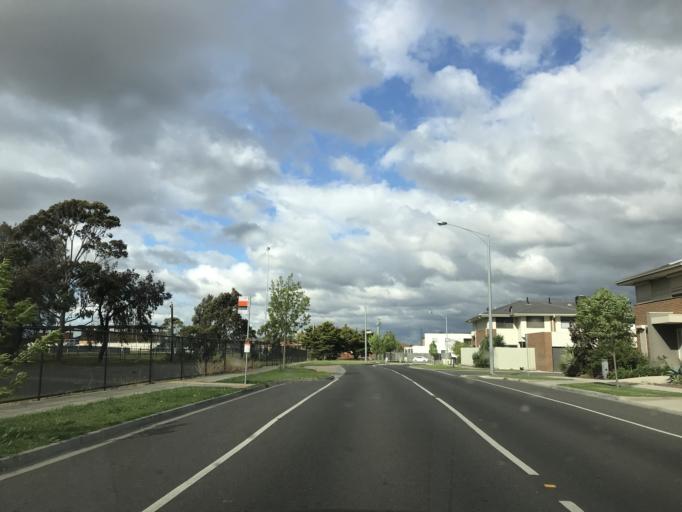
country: AU
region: Victoria
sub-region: Brimbank
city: Sunshine West
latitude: -37.7935
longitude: 144.7980
